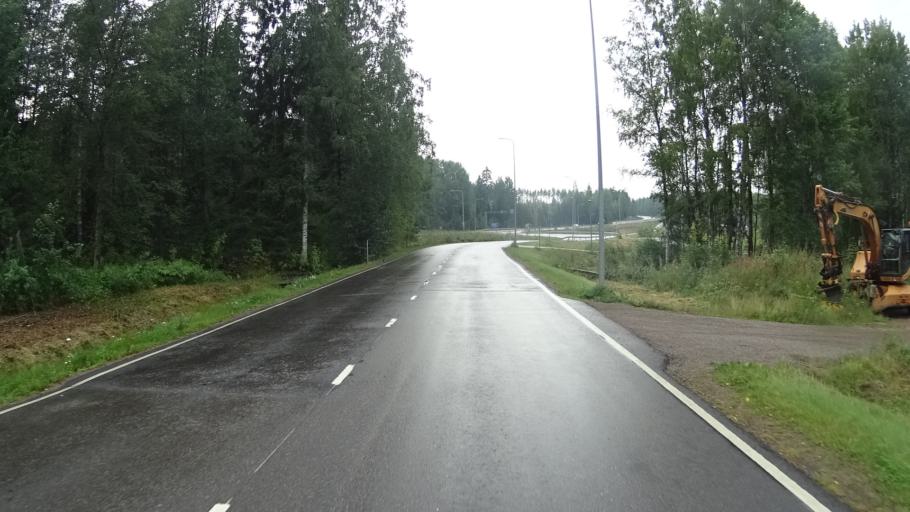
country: FI
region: Kymenlaakso
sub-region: Kouvola
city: Kouvola
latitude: 60.8883
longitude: 26.7635
